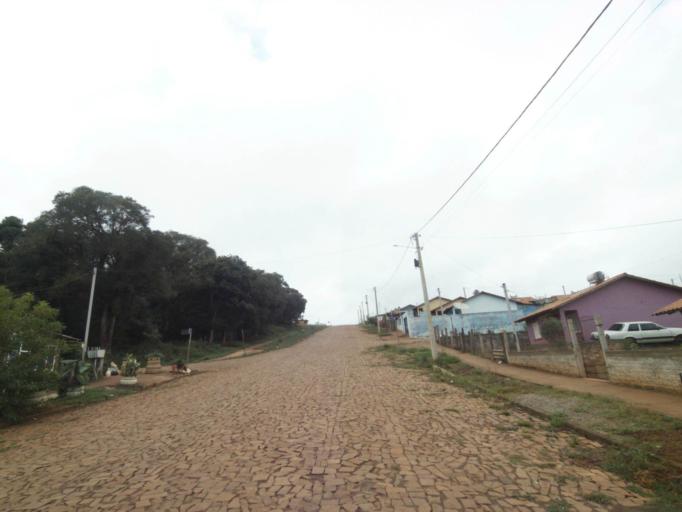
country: BR
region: Rio Grande do Sul
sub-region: Lagoa Vermelha
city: Lagoa Vermelha
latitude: -28.2237
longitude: -51.5186
